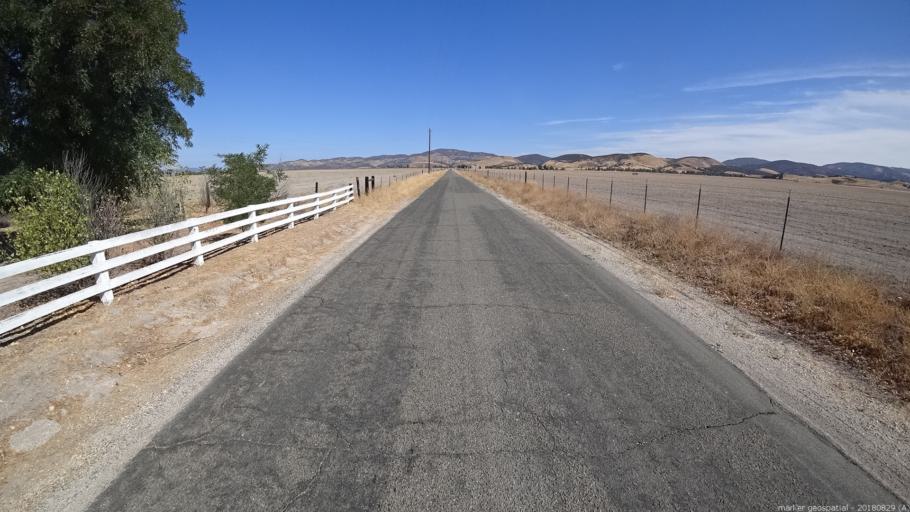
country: US
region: California
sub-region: Monterey County
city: King City
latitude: 35.9444
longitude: -121.0821
